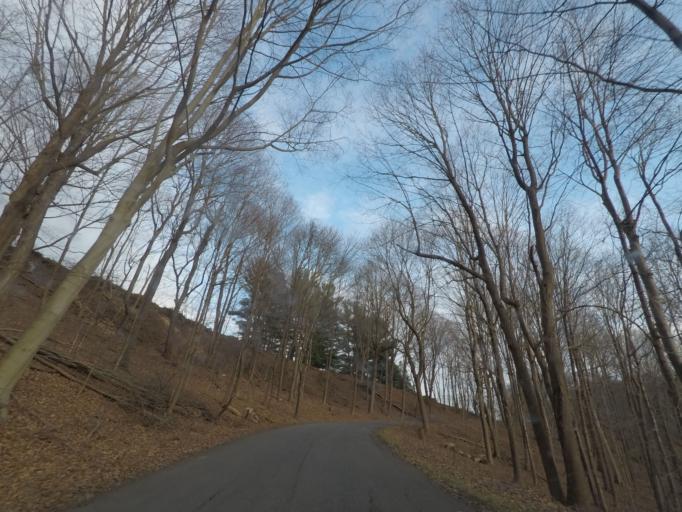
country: US
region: New York
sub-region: Rensselaer County
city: Wynantskill
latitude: 42.7239
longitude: -73.6450
